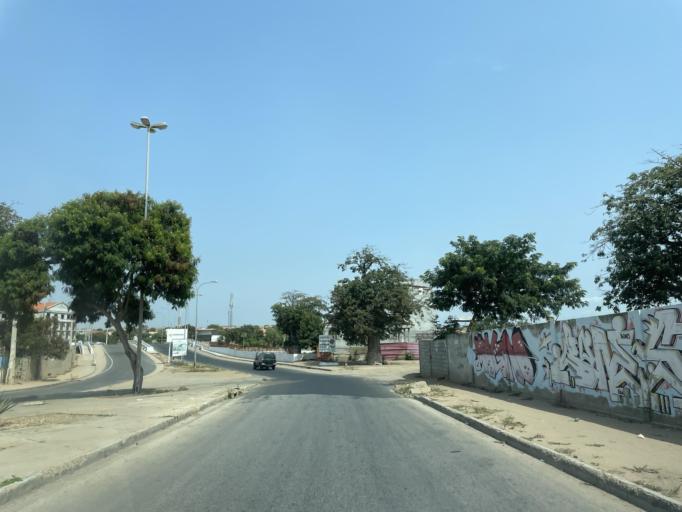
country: AO
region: Luanda
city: Luanda
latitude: -8.9264
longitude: 13.1960
